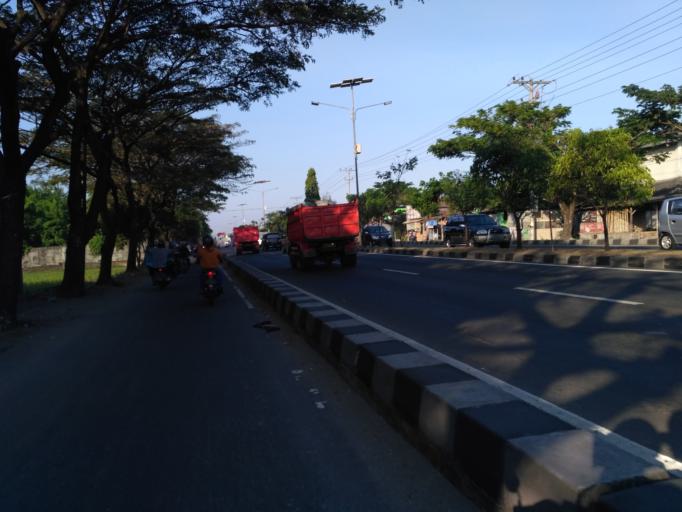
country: ID
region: Daerah Istimewa Yogyakarta
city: Sewon
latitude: -7.8359
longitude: 110.3782
